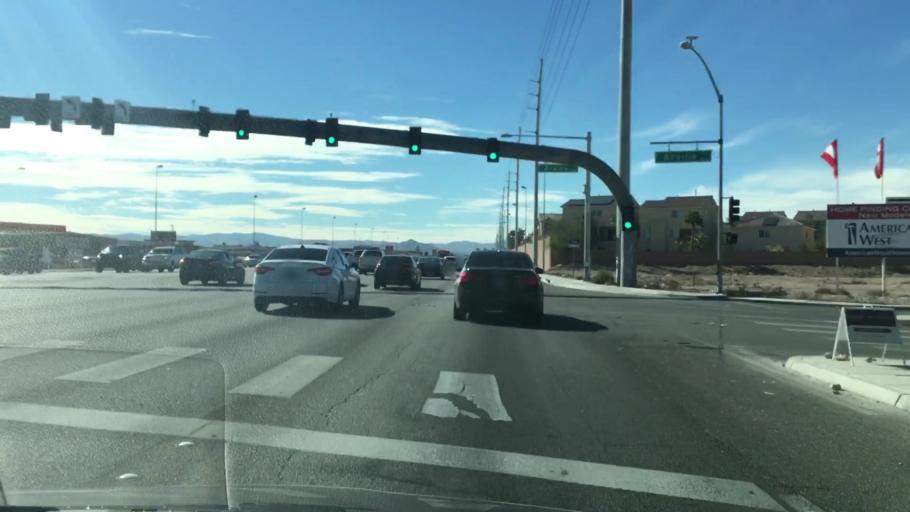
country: US
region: Nevada
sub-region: Clark County
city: Enterprise
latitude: 36.0368
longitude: -115.1990
